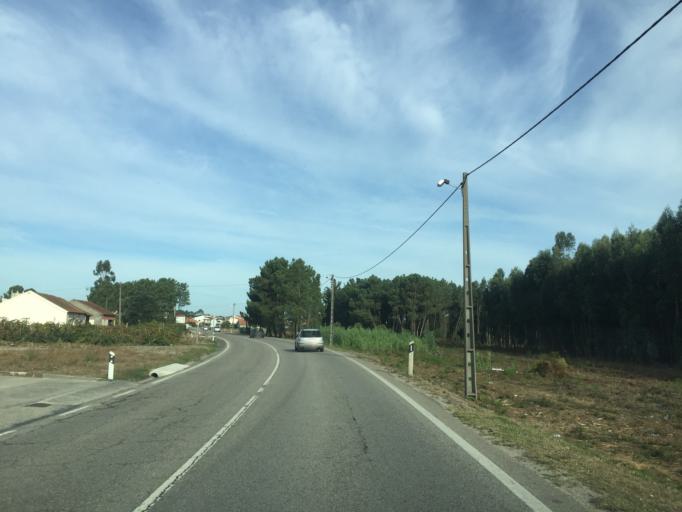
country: PT
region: Leiria
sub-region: Pombal
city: Lourical
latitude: 39.9717
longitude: -8.7934
